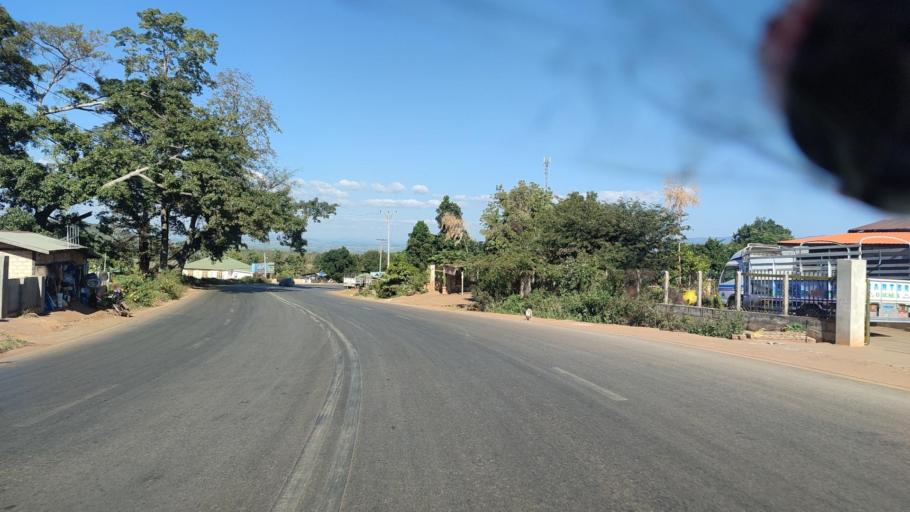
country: MM
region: Mandalay
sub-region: Pyin Oo Lwin District
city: Pyin Oo Lwin
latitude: 22.1608
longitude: 96.6191
